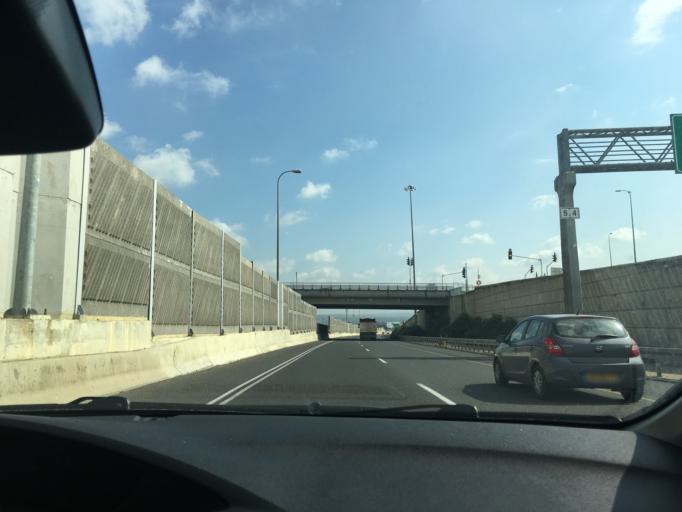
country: IL
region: Central District
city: Kfar Saba
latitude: 32.1686
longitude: 34.9108
